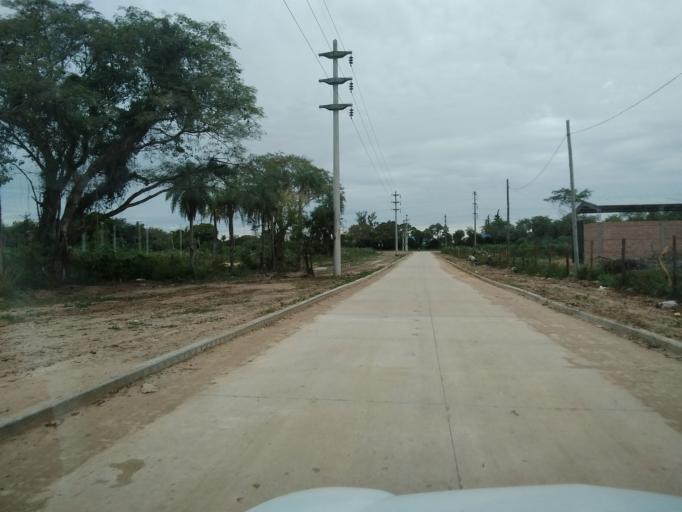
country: AR
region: Corrientes
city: Corrientes
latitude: -27.5155
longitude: -58.8213
